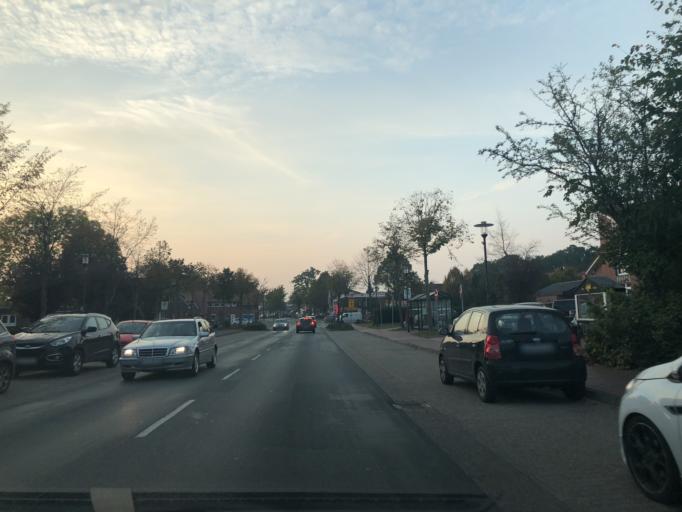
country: DE
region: Lower Saxony
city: Bosel
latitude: 53.0057
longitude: 7.9558
